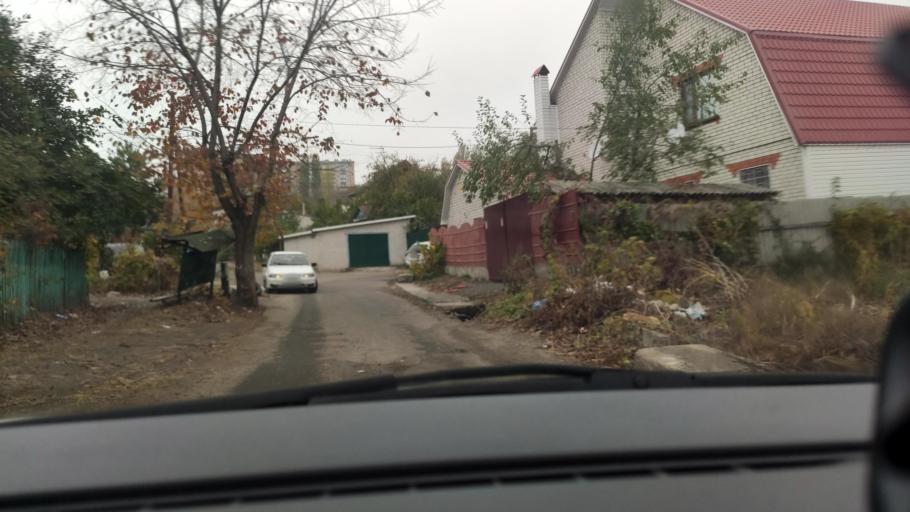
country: RU
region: Voronezj
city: Voronezh
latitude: 51.6856
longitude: 39.2250
